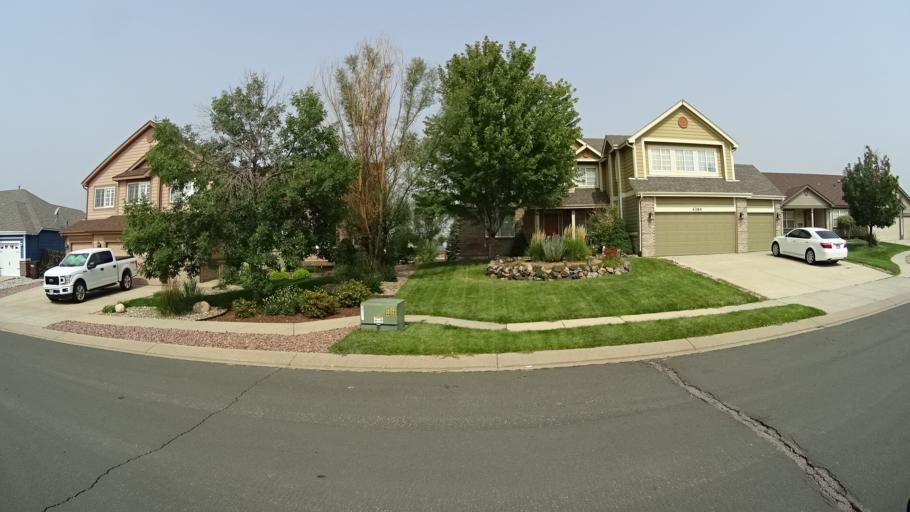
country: US
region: Colorado
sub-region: El Paso County
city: Cimarron Hills
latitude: 38.9275
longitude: -104.7474
